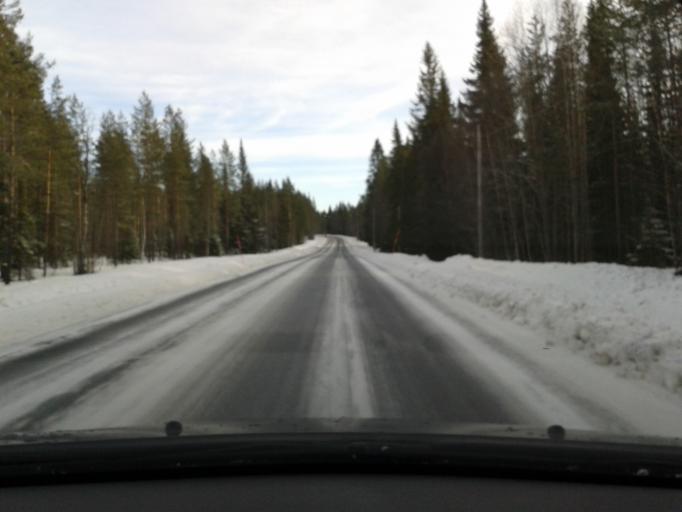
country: SE
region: Vaesterbotten
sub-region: Vilhelmina Kommun
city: Vilhelmina
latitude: 64.6476
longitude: 16.5220
